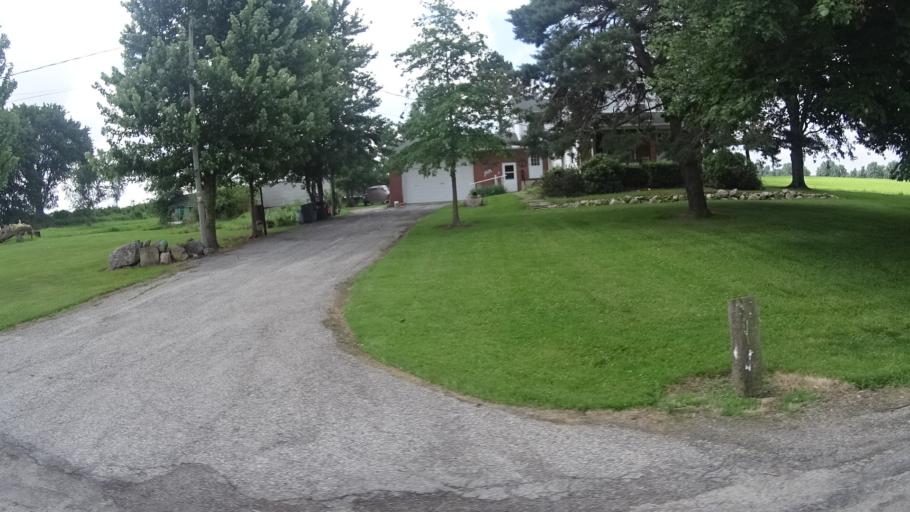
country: US
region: Ohio
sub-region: Huron County
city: Wakeman
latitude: 41.3058
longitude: -82.3989
